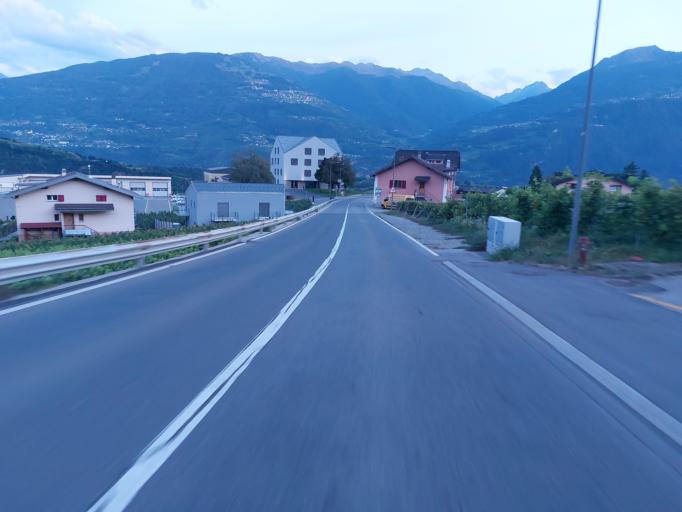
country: CH
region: Valais
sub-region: Conthey District
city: Conthey
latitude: 46.2362
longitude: 7.3043
